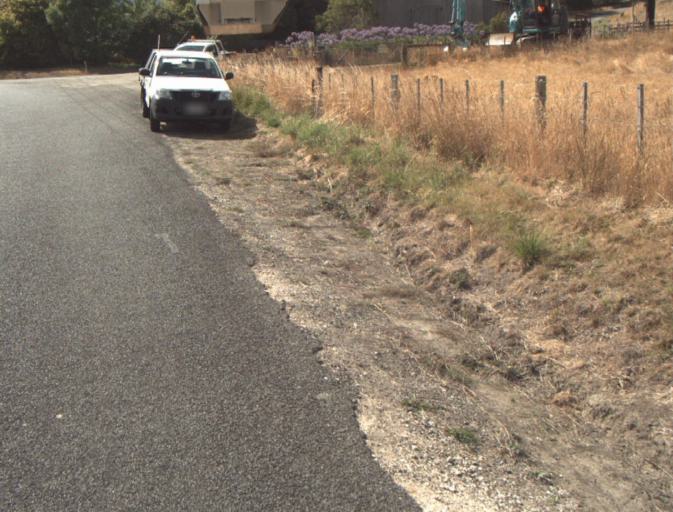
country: AU
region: Tasmania
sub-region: Launceston
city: Mayfield
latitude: -41.2582
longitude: 147.1914
